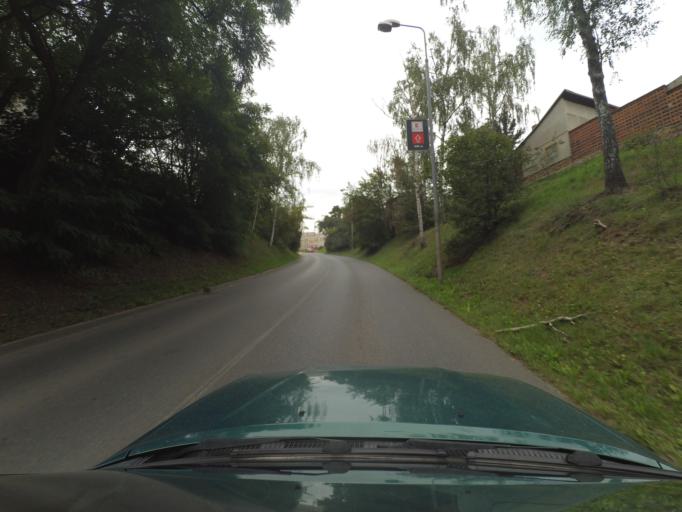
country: CZ
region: Central Bohemia
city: Rakovnik
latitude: 50.1082
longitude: 13.7341
